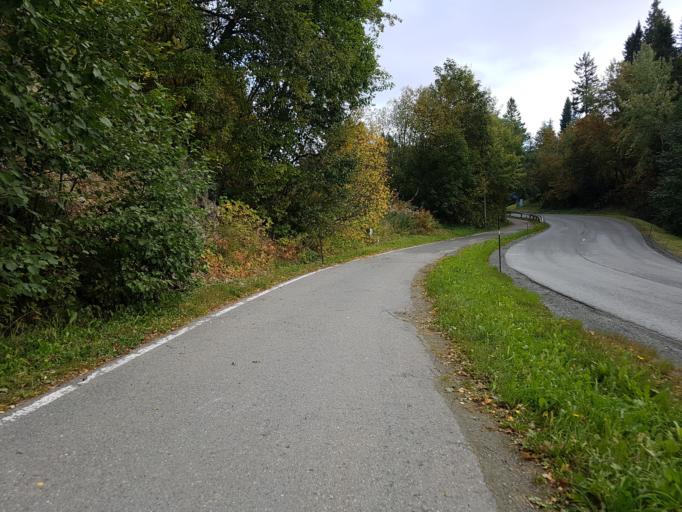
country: NO
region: Sor-Trondelag
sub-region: Klaebu
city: Klaebu
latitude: 63.4014
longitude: 10.5160
